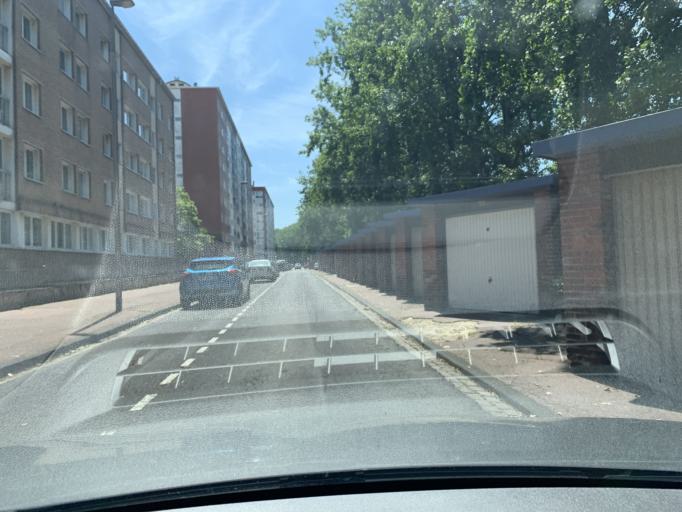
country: FR
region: Nord-Pas-de-Calais
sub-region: Departement du Nord
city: Dunkerque
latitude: 51.0427
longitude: 2.3870
